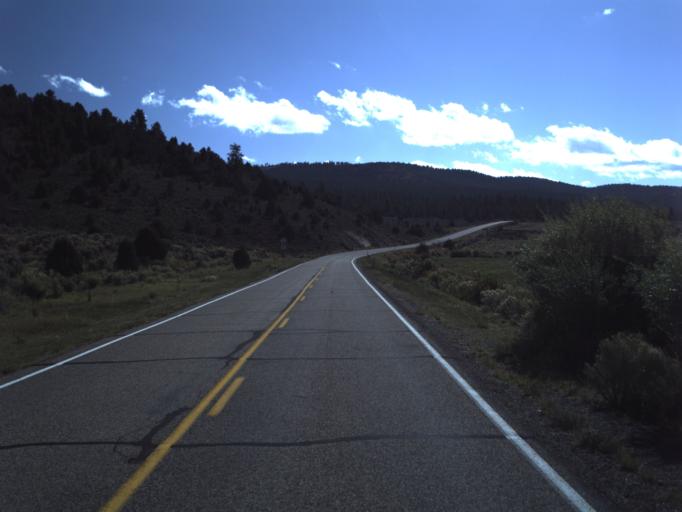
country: US
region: Utah
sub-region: Garfield County
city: Panguitch
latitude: 37.7599
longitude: -112.5598
